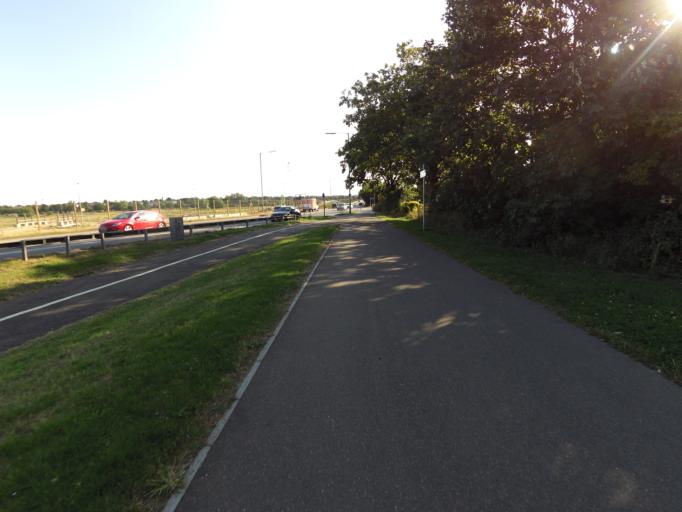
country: GB
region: England
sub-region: Essex
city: Chelmsford
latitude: 51.7311
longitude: 0.4917
